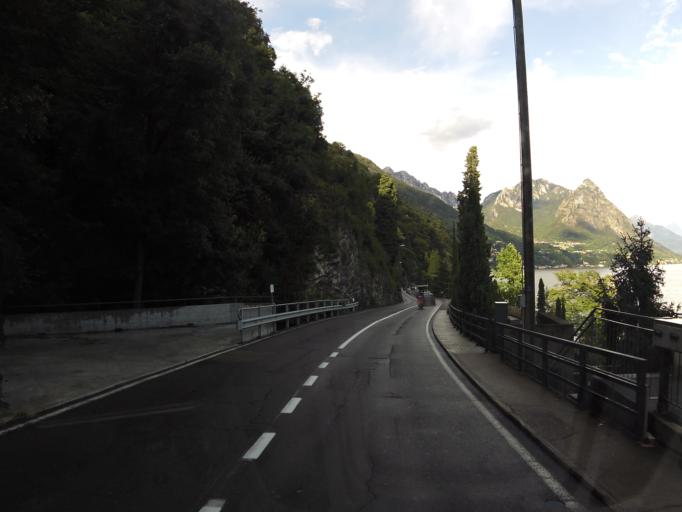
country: IT
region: Lombardy
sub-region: Provincia di Como
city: Lanzo d'Intelvi
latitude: 46.0103
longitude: 9.0108
